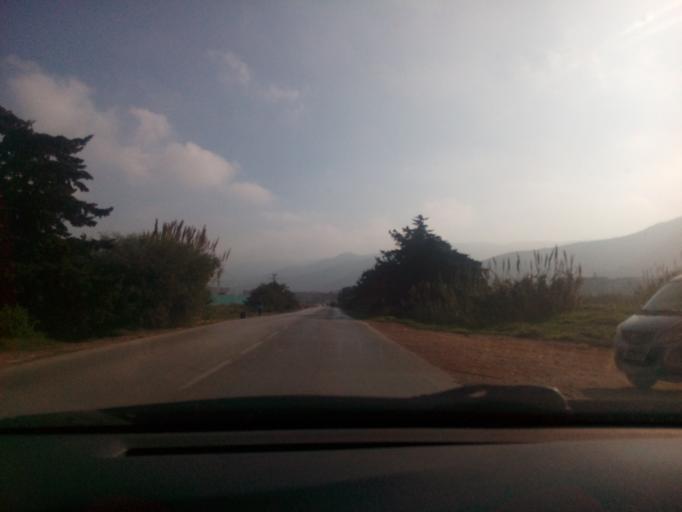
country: DZ
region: Oran
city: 'Ain el Turk
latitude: 35.7043
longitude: -0.8258
